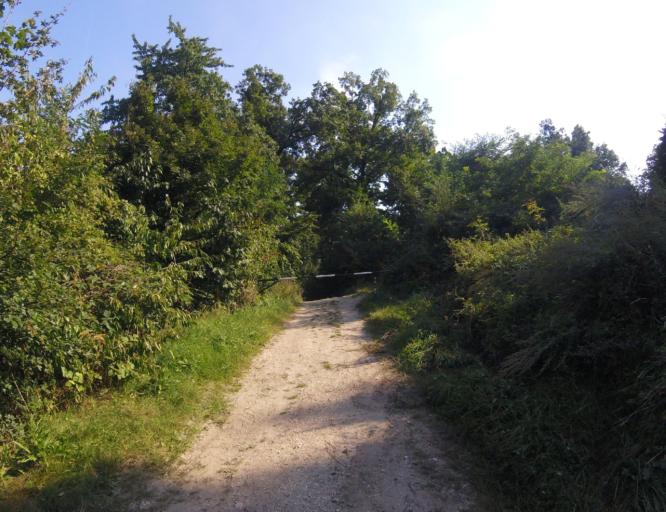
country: HU
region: Pest
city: Csobanka
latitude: 47.6881
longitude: 18.9857
